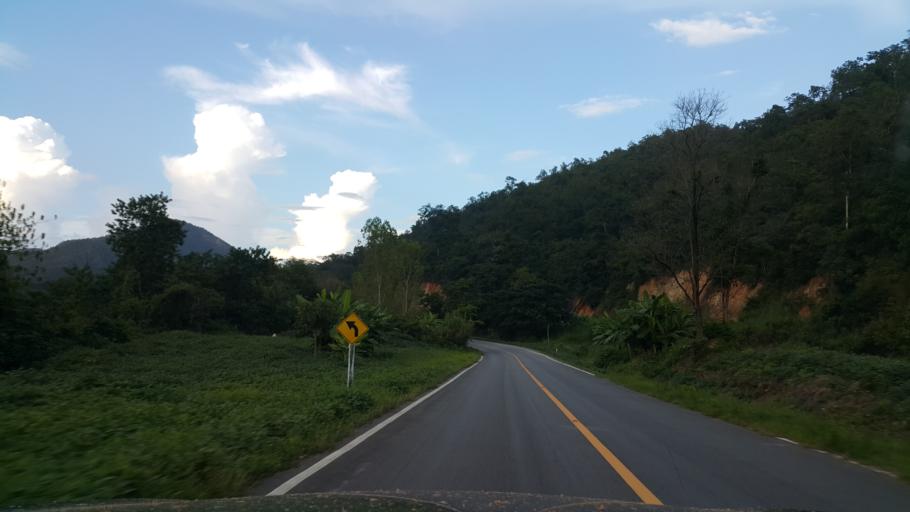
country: TH
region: Mae Hong Son
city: Mae Hi
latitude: 19.2363
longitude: 98.4479
